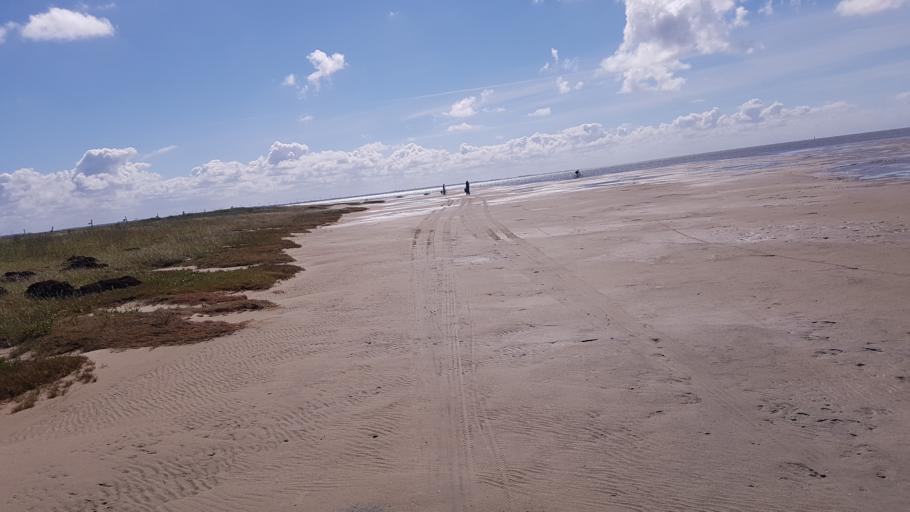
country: DE
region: Schleswig-Holstein
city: List
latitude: 55.0764
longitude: 8.5331
